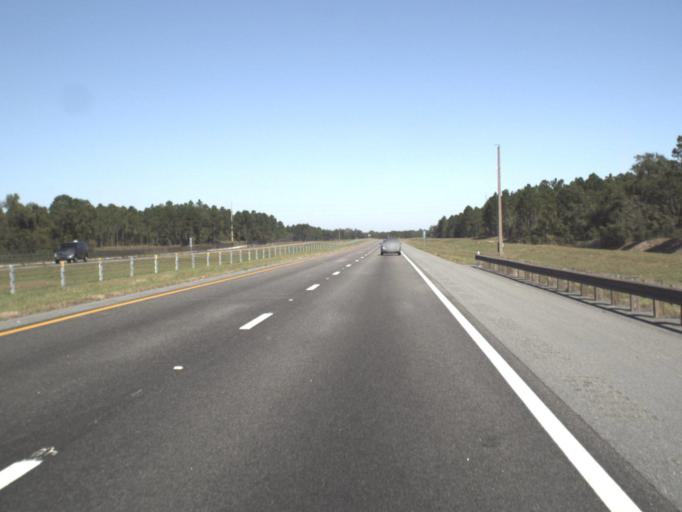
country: US
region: Florida
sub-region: Pasco County
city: Shady Hills
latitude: 28.3566
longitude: -82.5448
